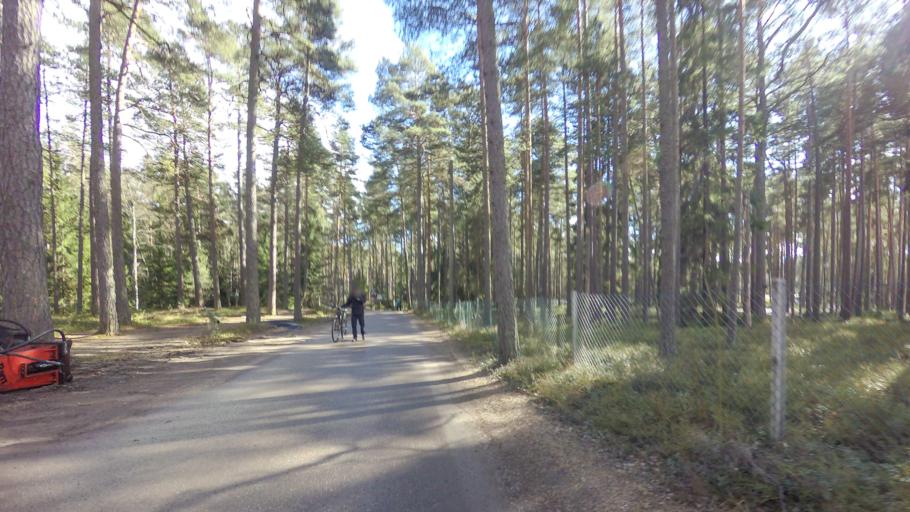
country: FI
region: Uusimaa
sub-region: Helsinki
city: Vantaa
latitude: 60.1915
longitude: 25.1380
